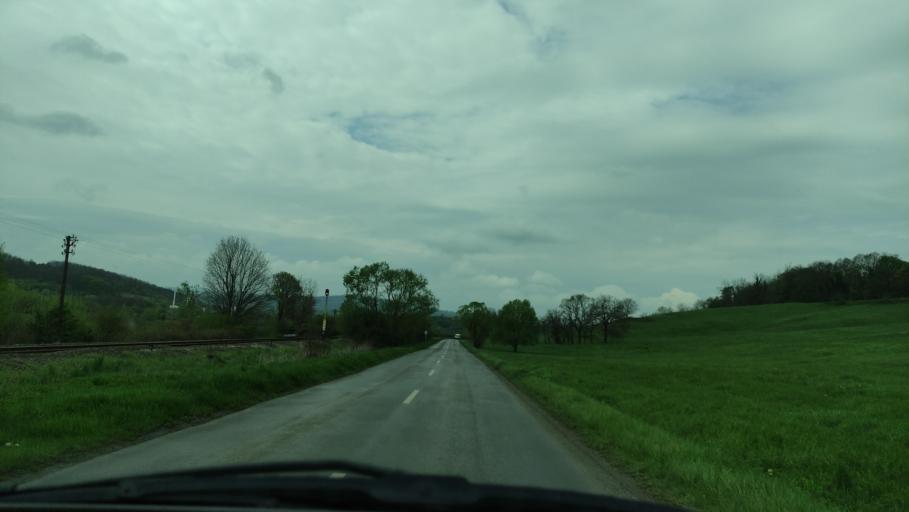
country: HU
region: Baranya
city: Komlo
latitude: 46.2162
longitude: 18.1943
